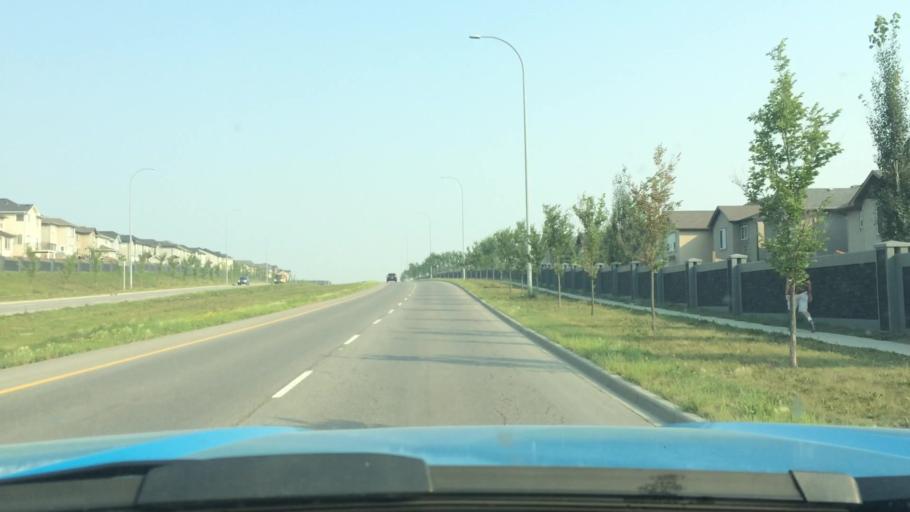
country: CA
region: Alberta
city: Calgary
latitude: 51.1757
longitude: -114.1569
